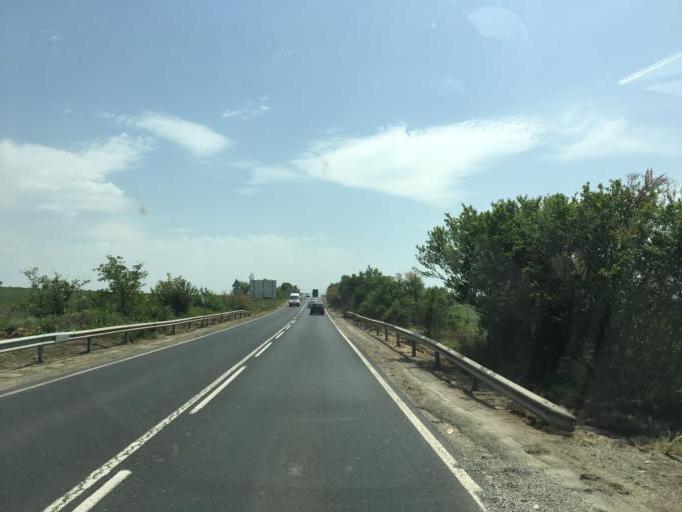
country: BG
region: Kyustendil
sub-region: Obshtina Kocherinovo
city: Kocherinovo
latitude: 42.0505
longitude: 23.0498
